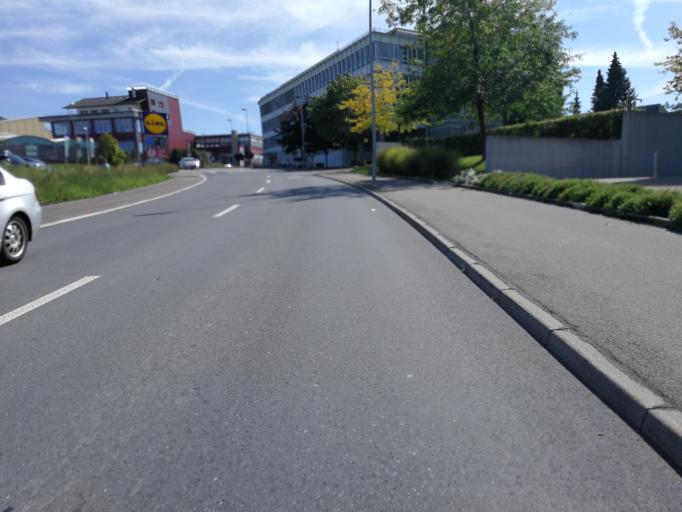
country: CH
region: Zurich
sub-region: Bezirk Horgen
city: Au
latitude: 47.2368
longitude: 8.6350
